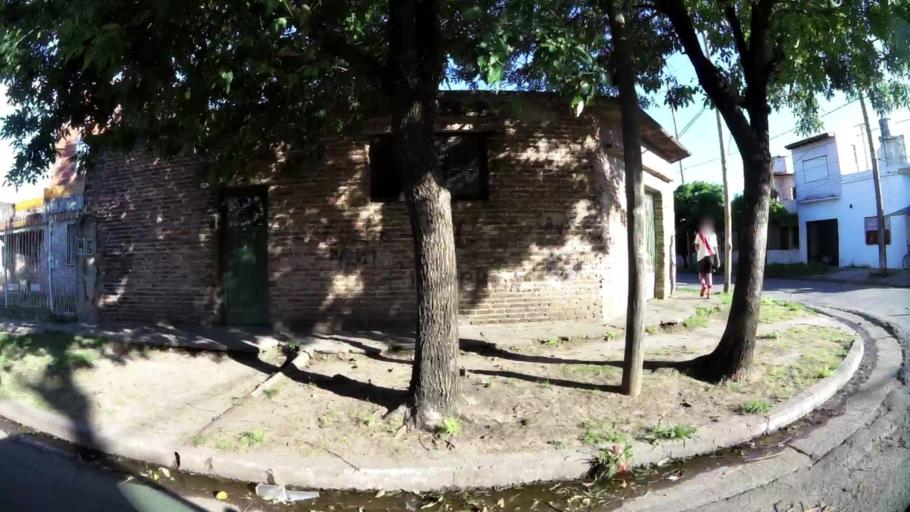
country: AR
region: Buenos Aires
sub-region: Partido de Moron
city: Moron
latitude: -34.6851
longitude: -58.6304
